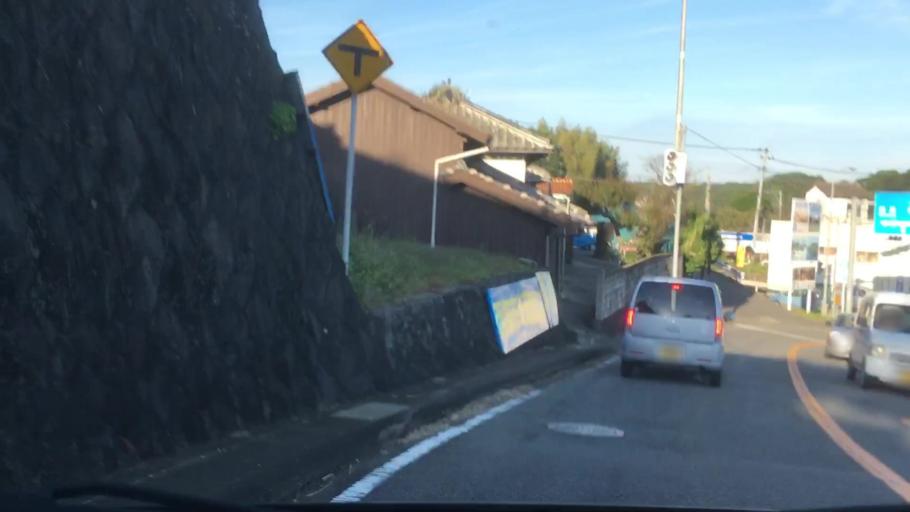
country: JP
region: Nagasaki
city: Sasebo
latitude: 33.0498
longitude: 129.7290
